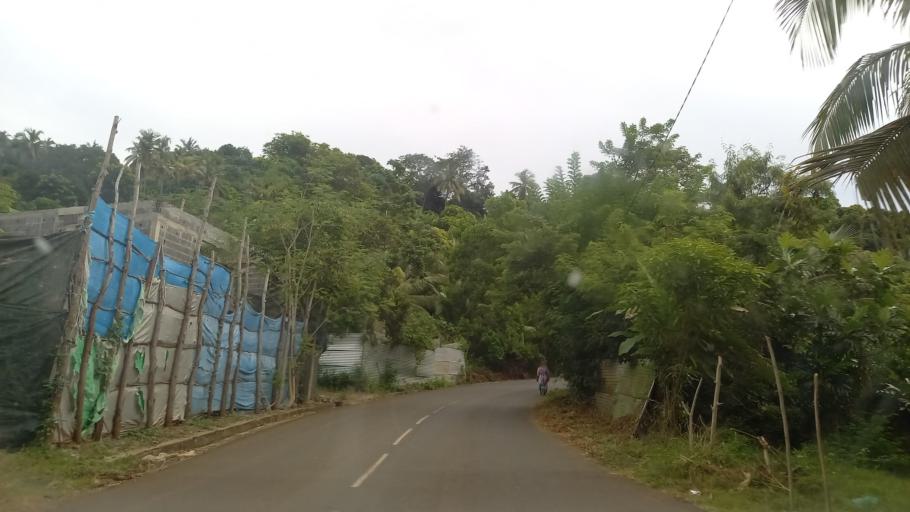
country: YT
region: Boueni
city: Boueni
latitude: -12.9017
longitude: 45.0922
